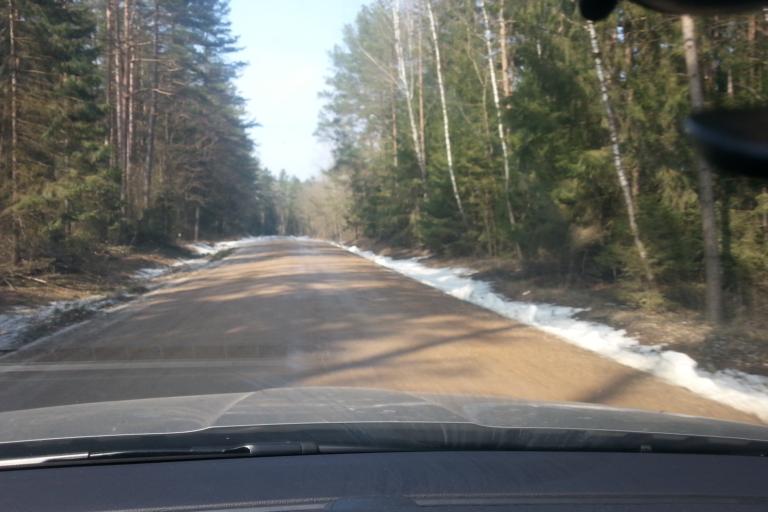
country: LT
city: Trakai
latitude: 54.5671
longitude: 24.9710
